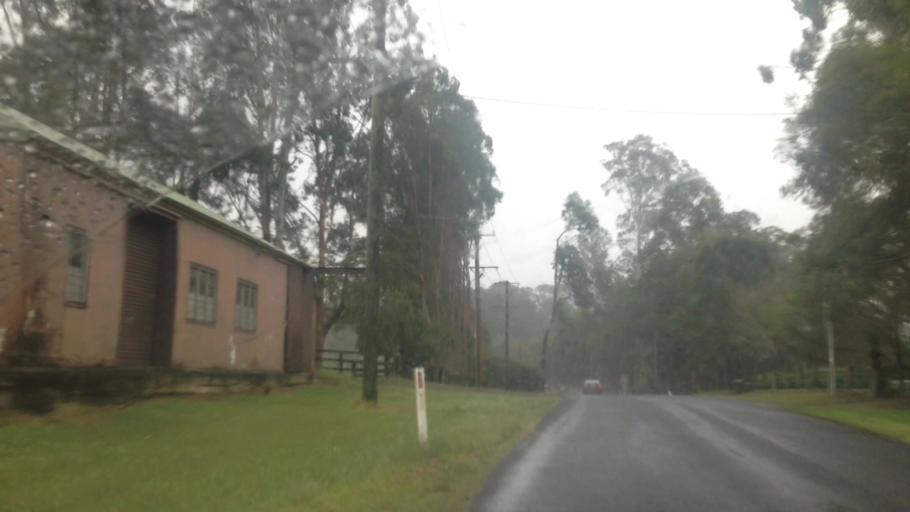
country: AU
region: New South Wales
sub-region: Wyong Shire
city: Little Jilliby
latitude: -33.2054
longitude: 151.3636
